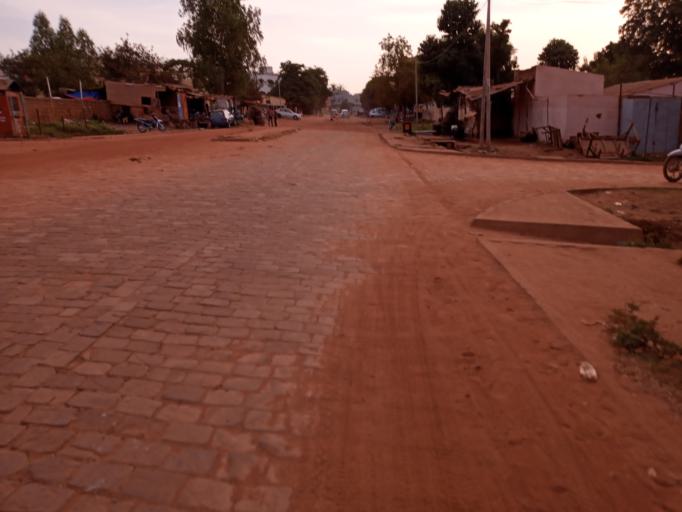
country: ML
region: Bamako
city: Bamako
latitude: 12.5935
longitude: -7.9580
